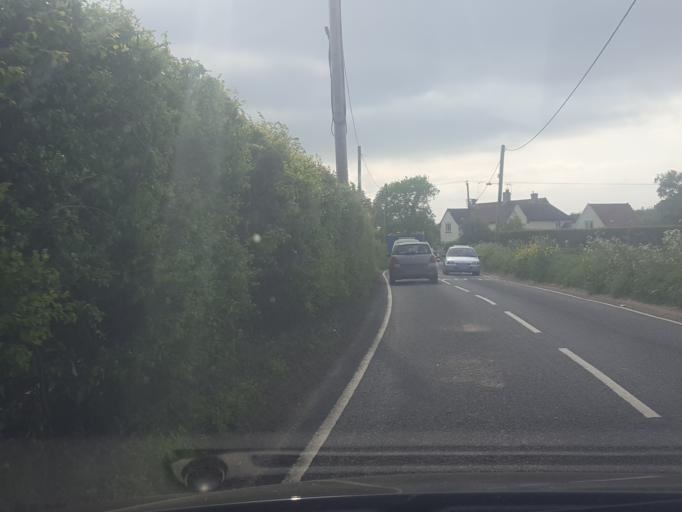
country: GB
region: England
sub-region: Essex
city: Frinton-on-Sea
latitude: 51.8265
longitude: 1.1992
